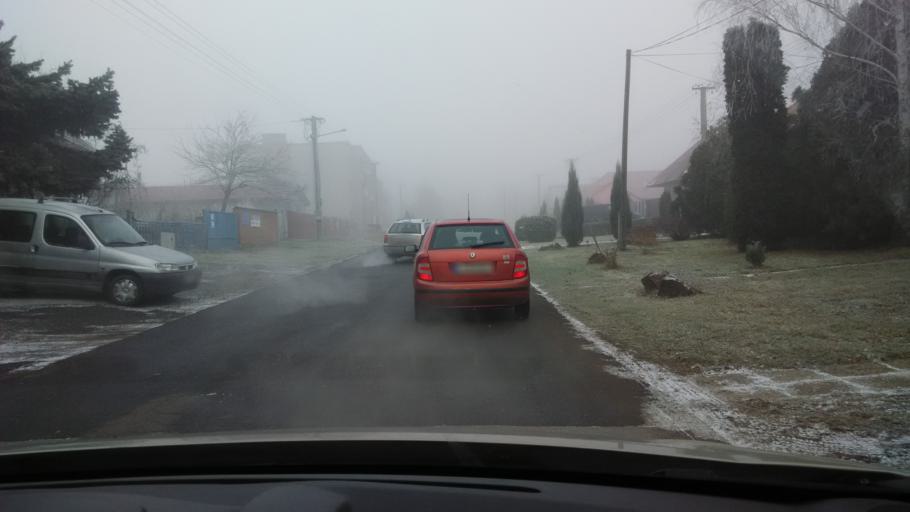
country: SK
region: Nitriansky
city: Tlmace
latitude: 48.2437
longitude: 18.5315
